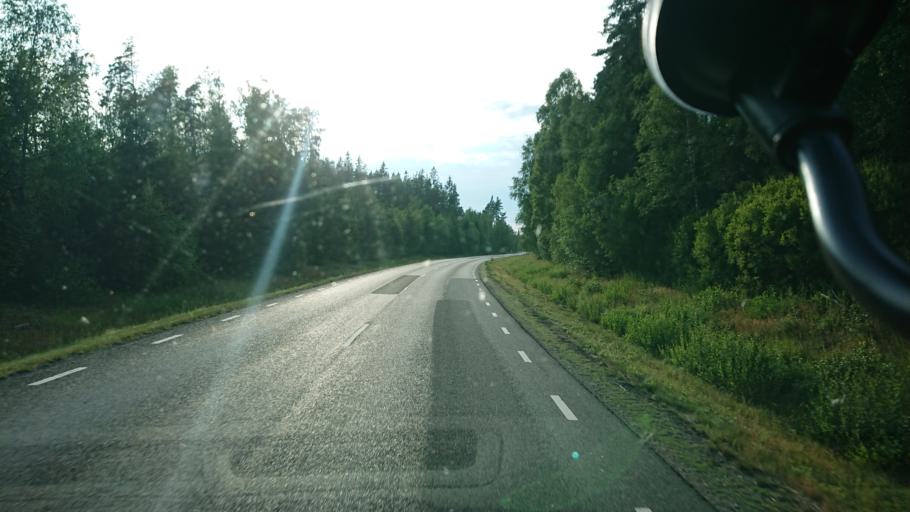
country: SE
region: Kronoberg
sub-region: Vaxjo Kommun
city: Braas
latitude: 57.0226
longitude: 15.0100
